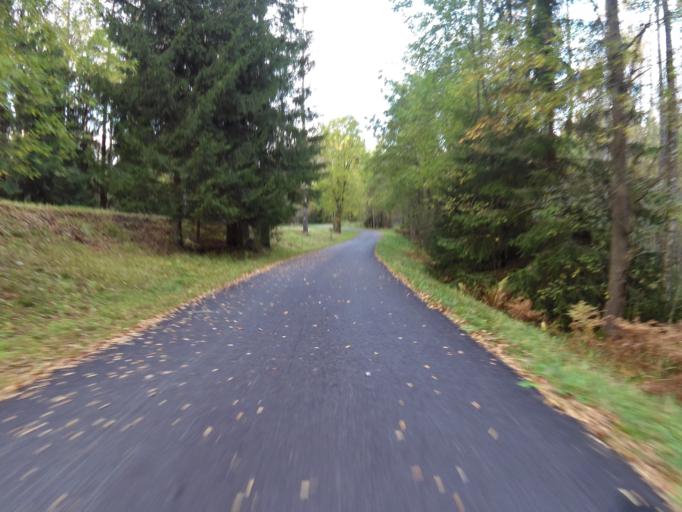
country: FI
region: Uusimaa
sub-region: Helsinki
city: Kauniainen
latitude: 60.2877
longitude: 24.7459
